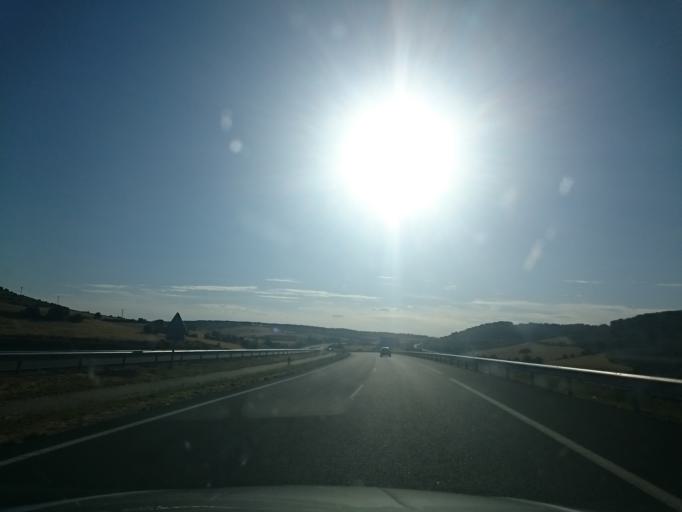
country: ES
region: Castille and Leon
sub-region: Provincia de Burgos
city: Villanueva de Argano
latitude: 42.3801
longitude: -3.9419
